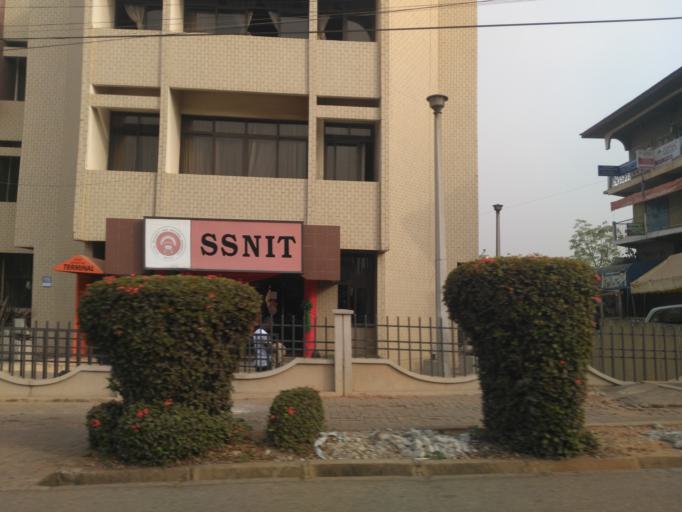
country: GH
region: Ashanti
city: Kumasi
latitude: 6.6896
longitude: -1.6108
